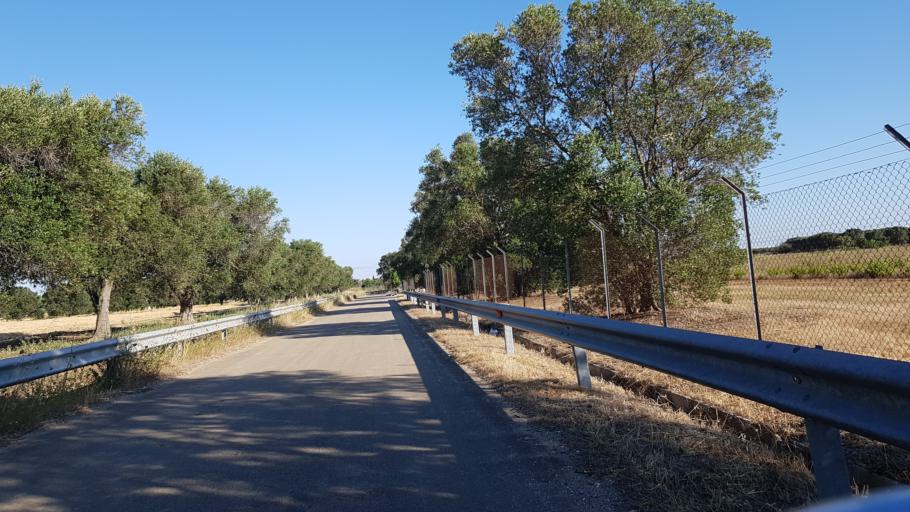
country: IT
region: Apulia
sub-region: Provincia di Brindisi
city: Tuturano
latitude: 40.5637
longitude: 18.0169
